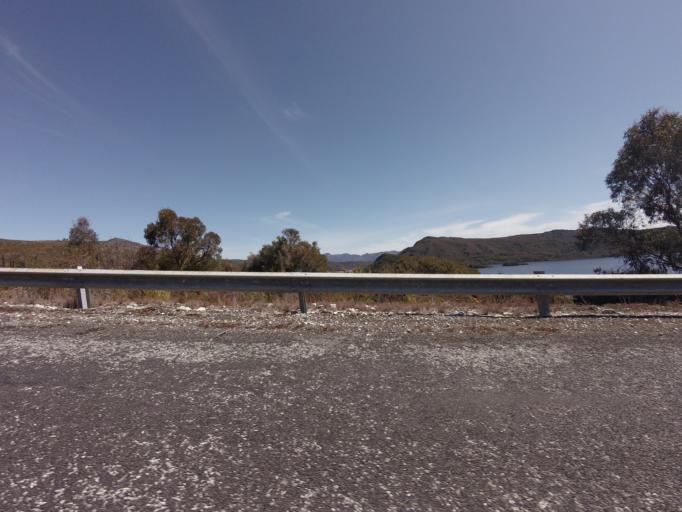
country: AU
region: Tasmania
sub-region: Huon Valley
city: Geeveston
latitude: -42.8357
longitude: 146.1277
